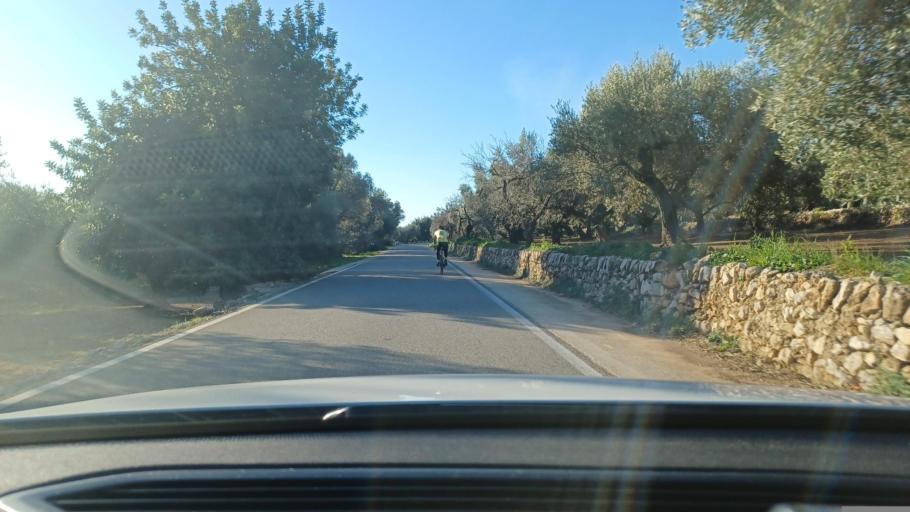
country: ES
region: Catalonia
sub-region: Provincia de Tarragona
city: Mas de Barberans
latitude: 40.7251
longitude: 0.3678
